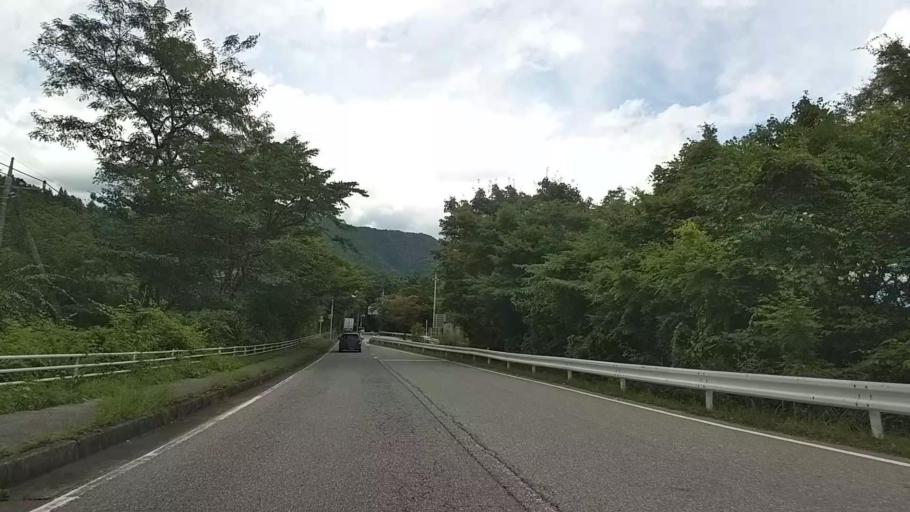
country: JP
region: Tochigi
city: Nikko
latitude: 36.7416
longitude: 139.5665
